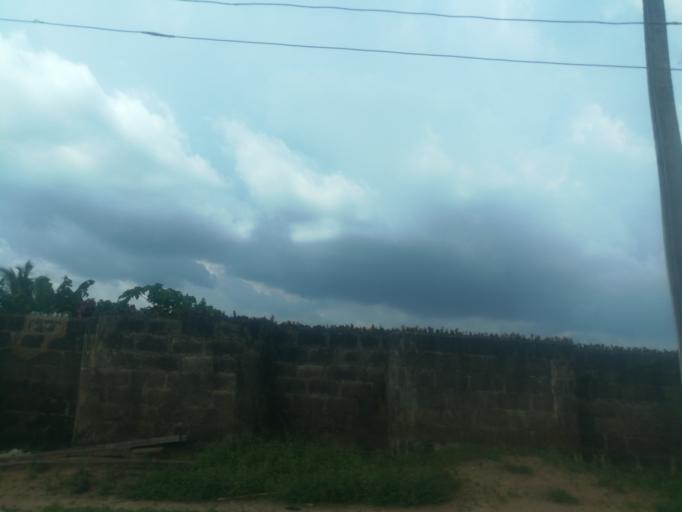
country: NG
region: Oyo
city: Ibadan
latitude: 7.4069
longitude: 3.8297
